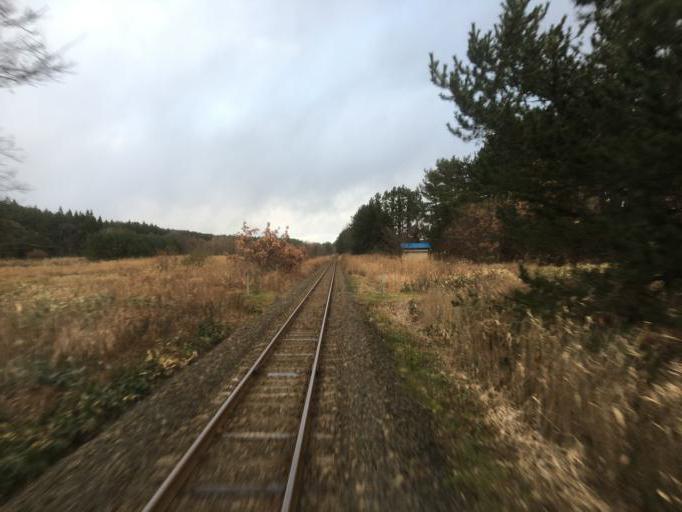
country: JP
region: Aomori
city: Mutsu
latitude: 41.2332
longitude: 141.2457
